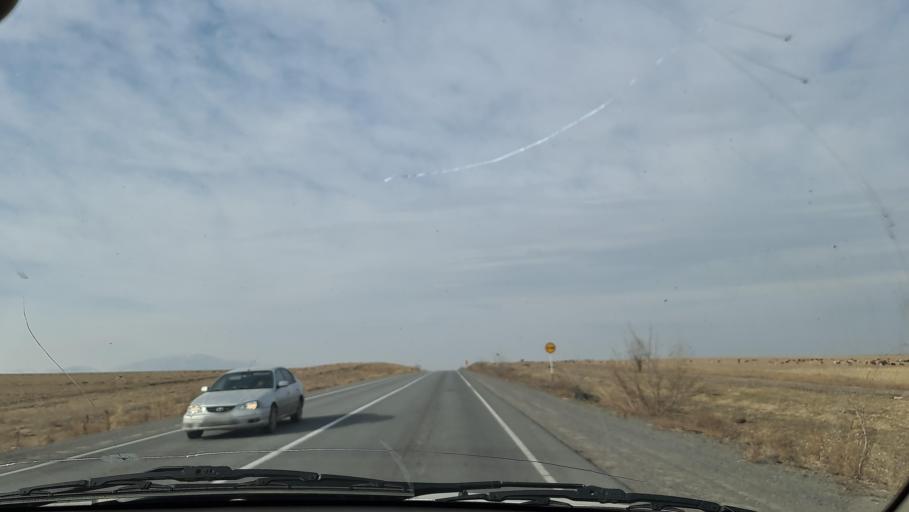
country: KG
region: Chuy
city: Bystrovka
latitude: 43.3225
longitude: 75.7174
